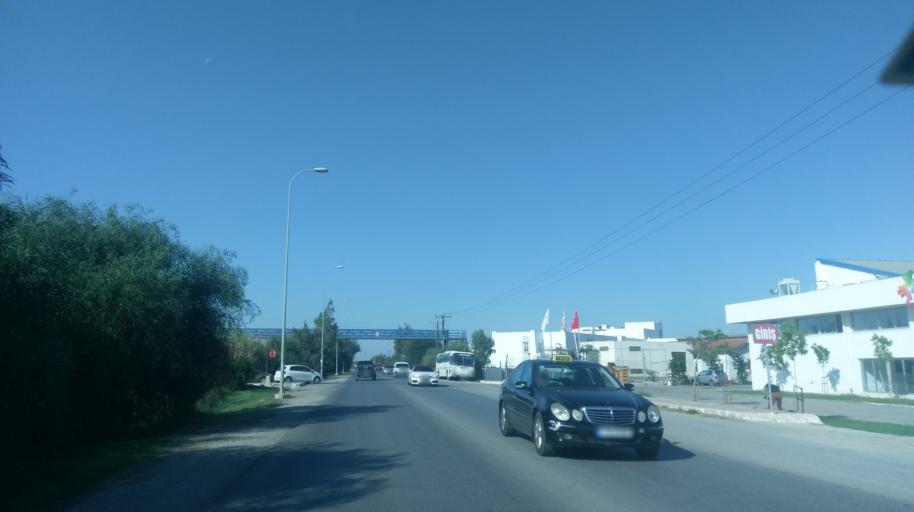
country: CY
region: Ammochostos
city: Famagusta
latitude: 35.1427
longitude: 33.9010
